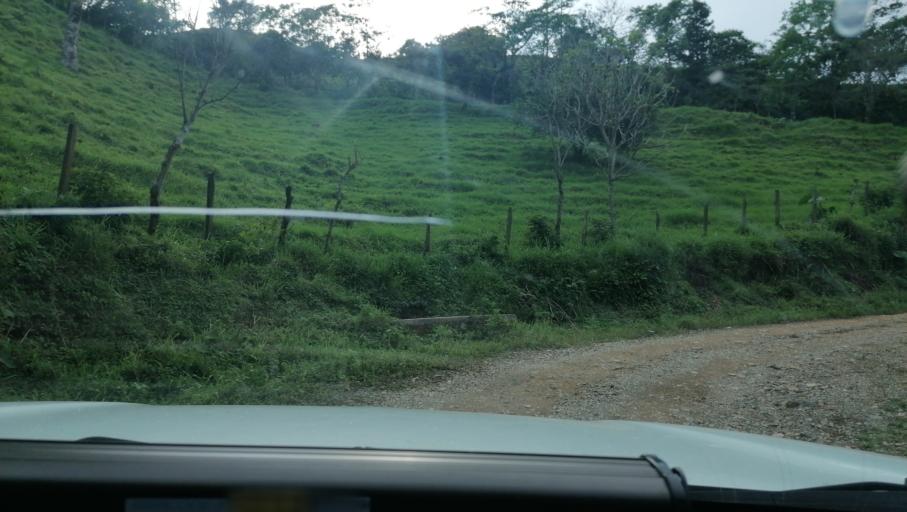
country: MX
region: Chiapas
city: Ixtacomitan
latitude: 17.3364
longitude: -93.1103
